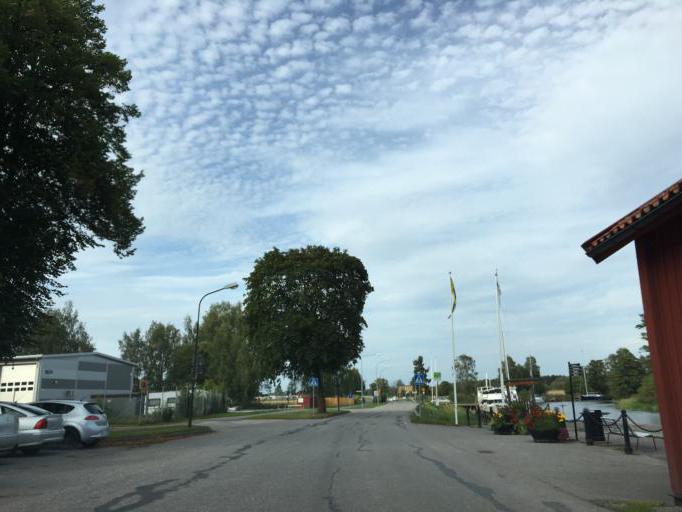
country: SE
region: Soedermanland
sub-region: Eskilstuna Kommun
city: Torshalla
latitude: 59.4270
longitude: 16.4722
